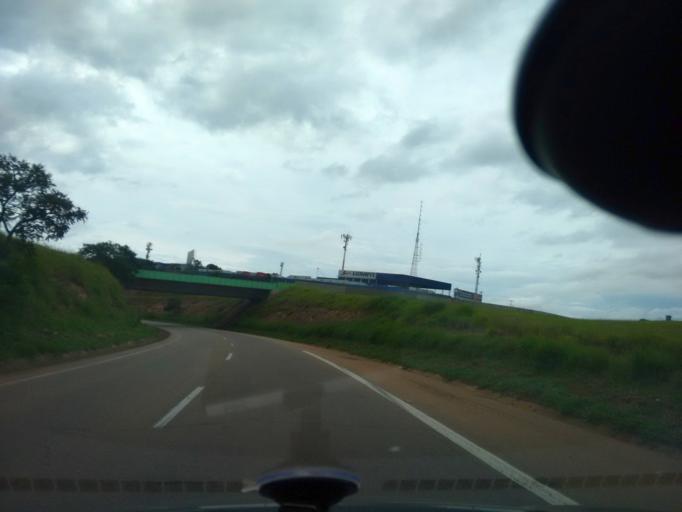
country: BR
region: Sao Paulo
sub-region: Campinas
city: Campinas
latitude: -22.9910
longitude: -47.1082
